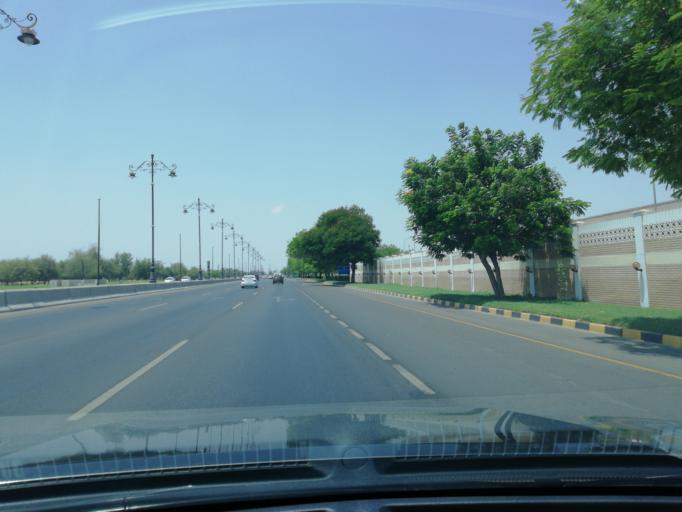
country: OM
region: Muhafazat Masqat
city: As Sib al Jadidah
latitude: 23.5836
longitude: 58.2727
